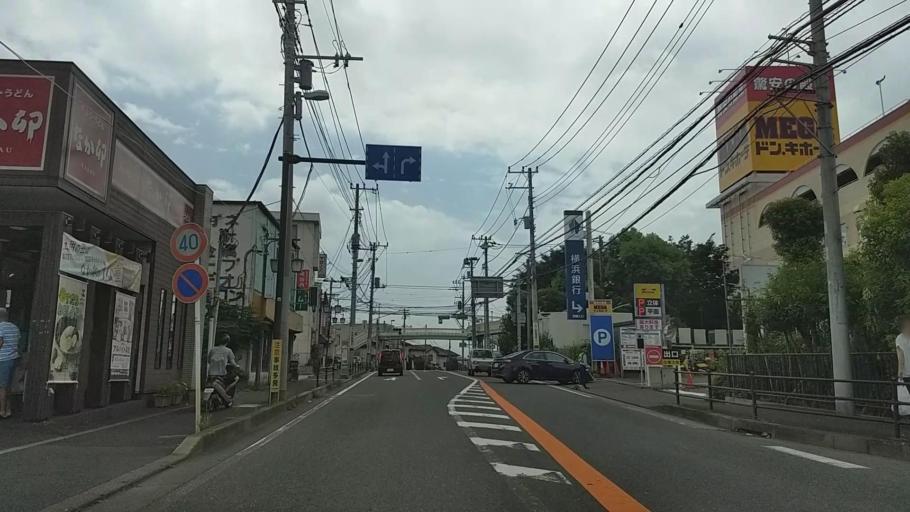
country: JP
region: Kanagawa
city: Minami-rinkan
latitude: 35.4573
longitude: 139.4278
